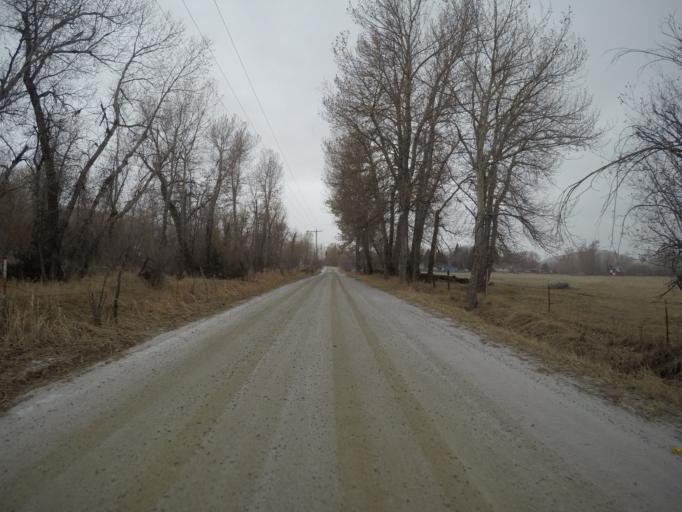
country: US
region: Montana
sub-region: Stillwater County
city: Absarokee
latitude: 45.5287
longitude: -109.4386
